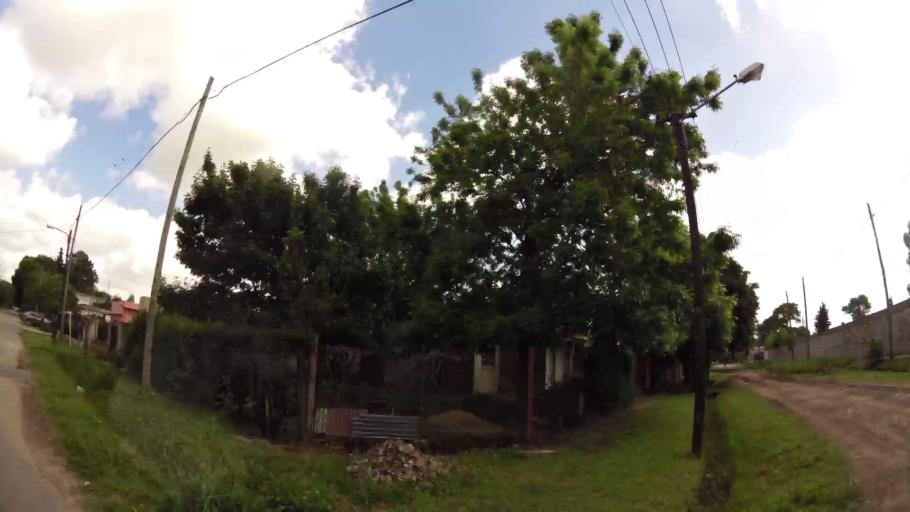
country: AR
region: Buenos Aires
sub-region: Partido de Quilmes
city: Quilmes
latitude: -34.8301
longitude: -58.1864
